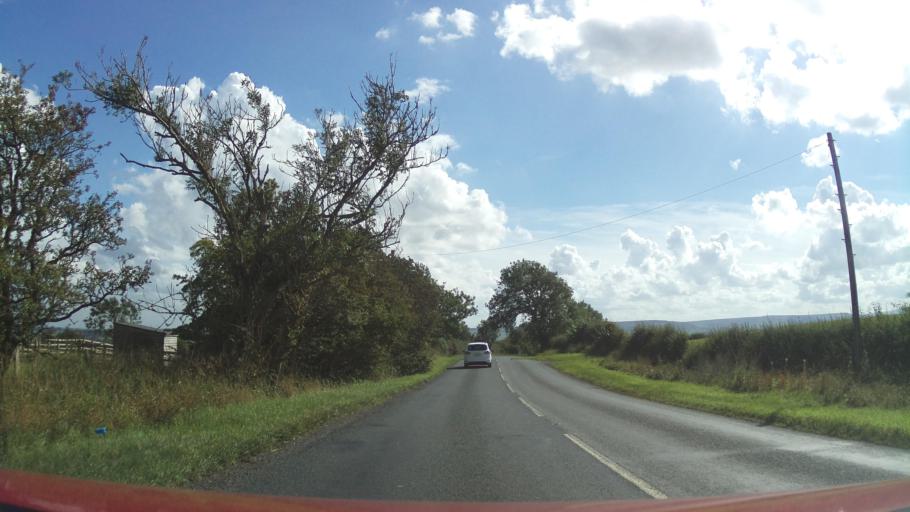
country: GB
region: England
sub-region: North Yorkshire
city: Leyburn
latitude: 54.3387
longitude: -1.8194
